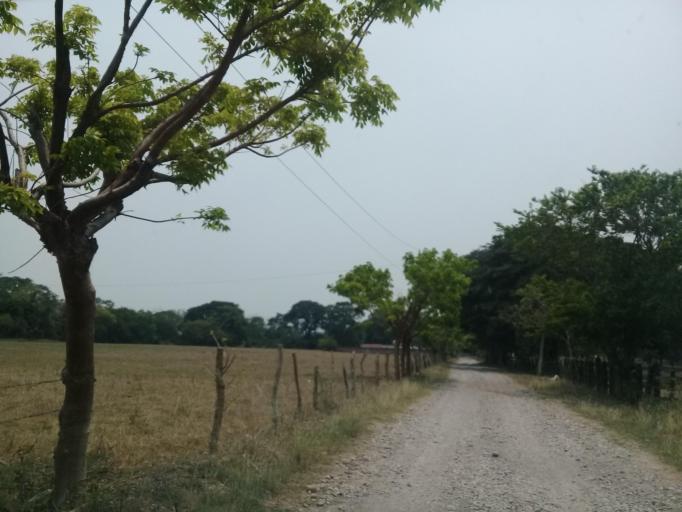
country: MX
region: Veracruz
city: Jamapa
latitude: 18.9324
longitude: -96.2088
